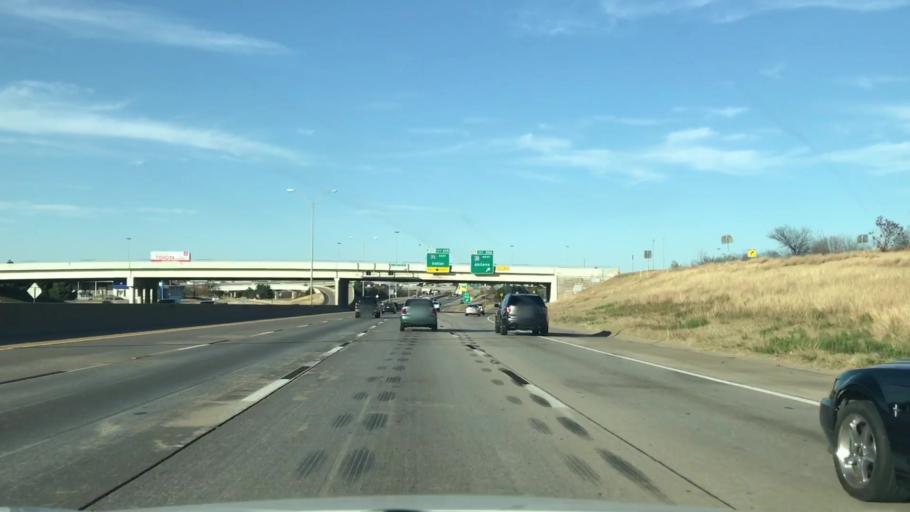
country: US
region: Texas
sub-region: Tarrant County
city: Edgecliff Village
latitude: 32.6592
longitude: -97.3212
